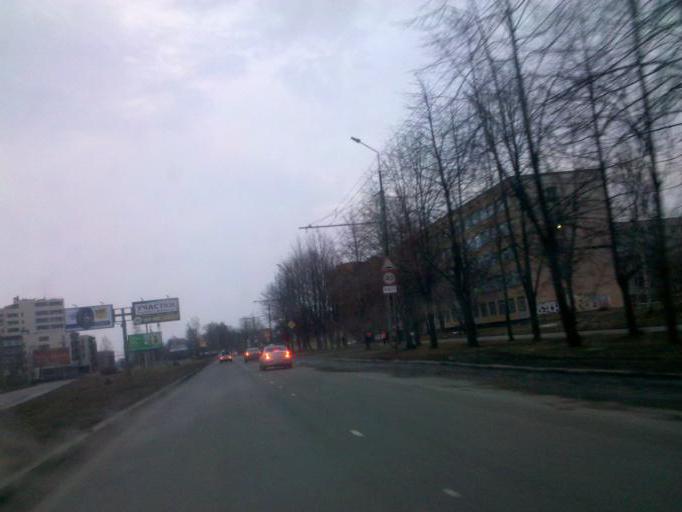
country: RU
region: Republic of Karelia
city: Petrozavodsk
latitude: 61.8012
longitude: 34.3559
